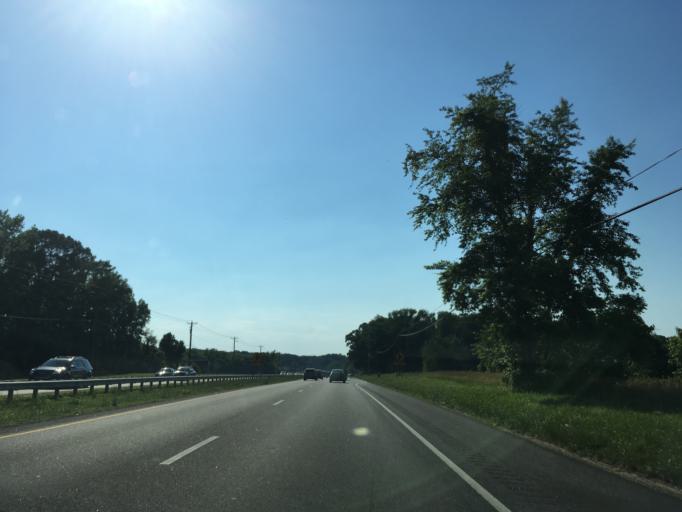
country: US
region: Maryland
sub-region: Queen Anne's County
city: Grasonville
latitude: 38.9782
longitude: -76.1353
